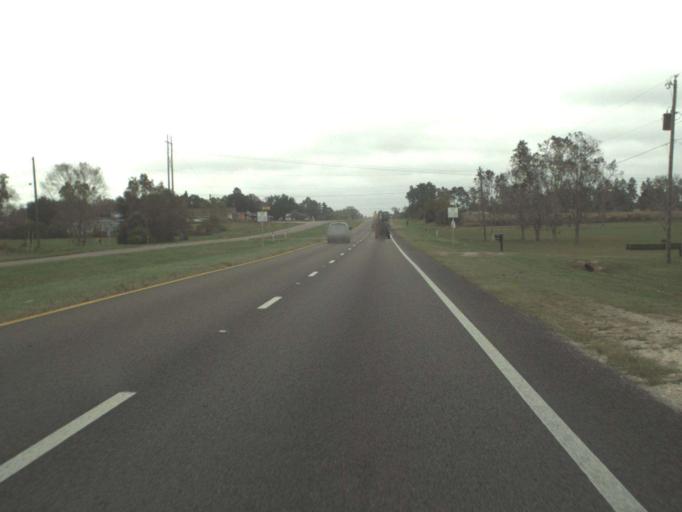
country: US
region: Florida
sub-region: Escambia County
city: Molino
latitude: 30.6973
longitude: -87.3505
